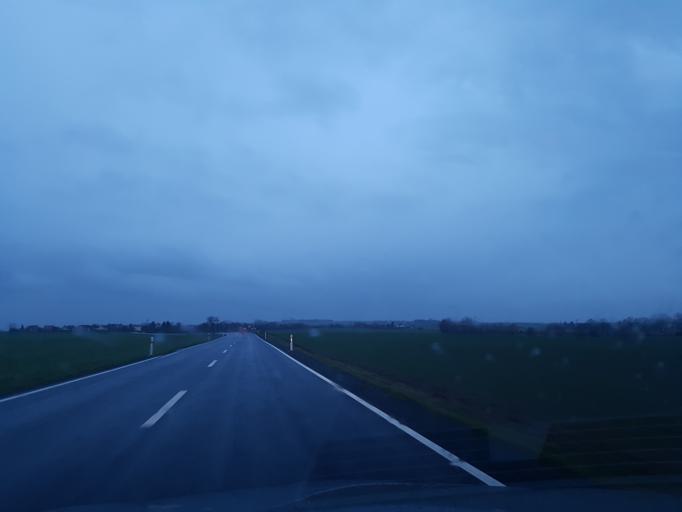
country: DE
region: Saxony
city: Priestewitz
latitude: 51.2643
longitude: 13.5138
